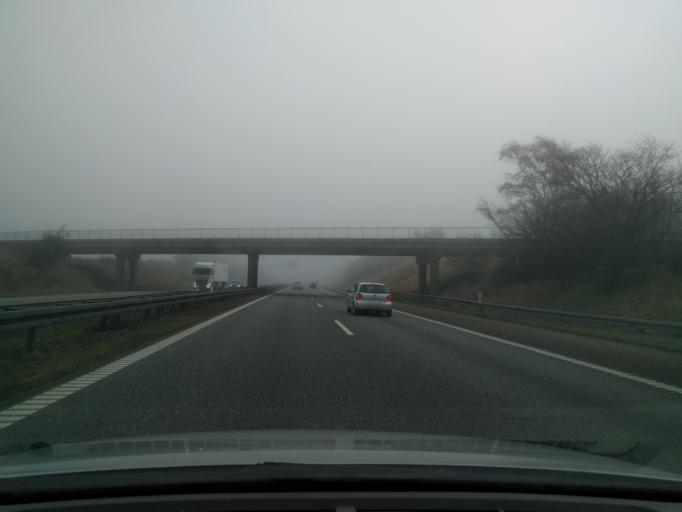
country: DK
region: Zealand
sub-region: Slagelse Kommune
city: Forlev
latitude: 55.3748
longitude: 11.3088
